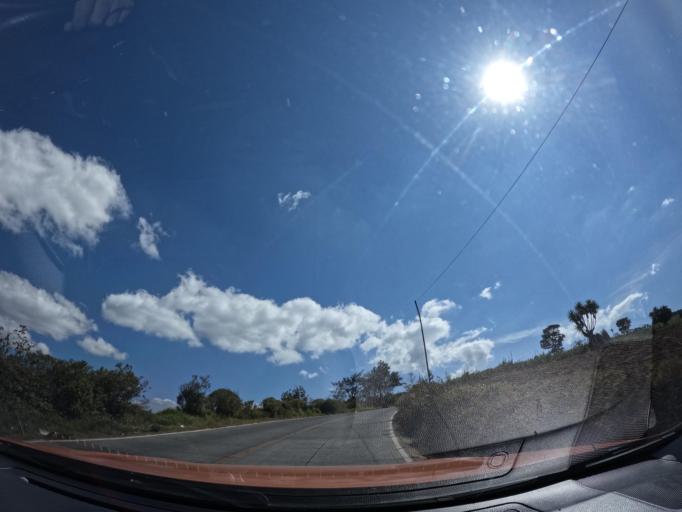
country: GT
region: Chimaltenango
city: Patzun
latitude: 14.6641
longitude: -91.0551
